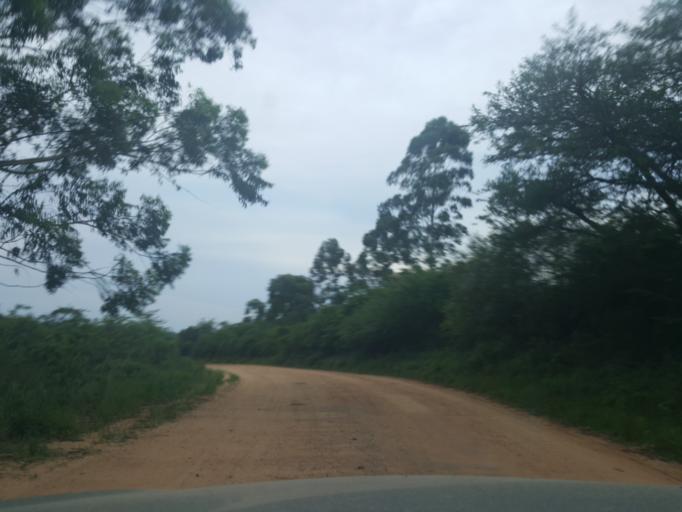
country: ZA
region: Limpopo
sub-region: Mopani District Municipality
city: Hoedspruit
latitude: -24.5978
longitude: 30.9251
